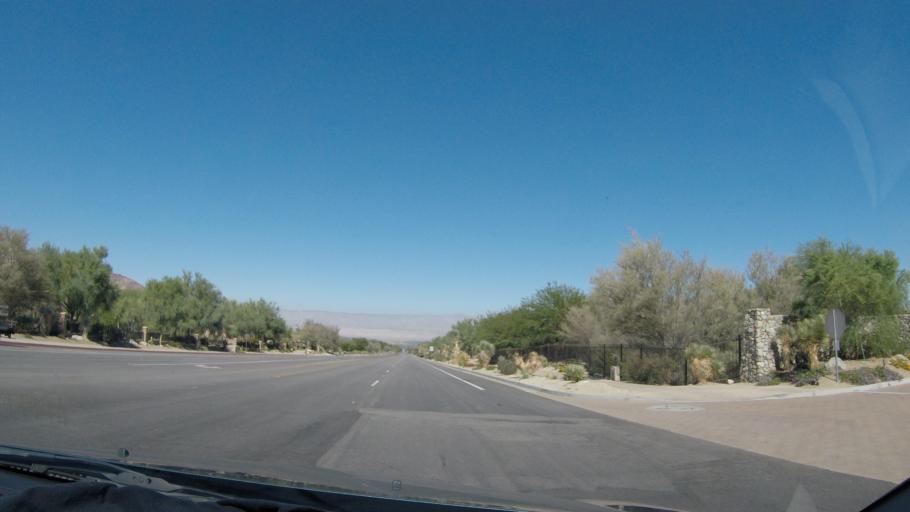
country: US
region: California
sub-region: Riverside County
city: Palm Desert
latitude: 33.6775
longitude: -116.4072
